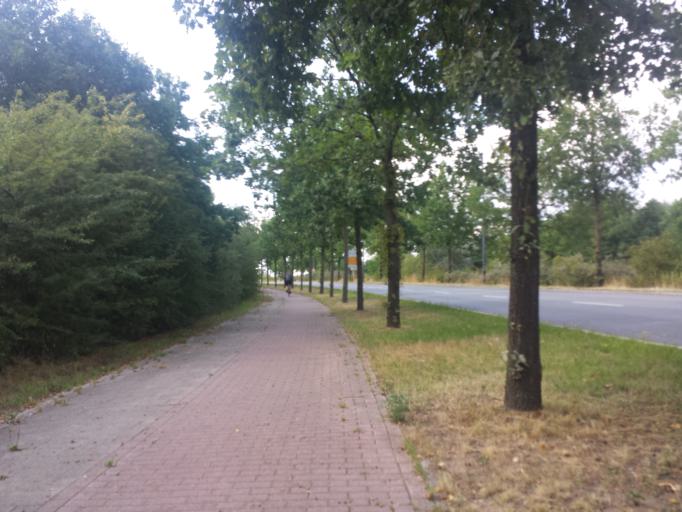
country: DE
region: Lower Saxony
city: Stuhr
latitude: 53.0846
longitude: 8.7317
